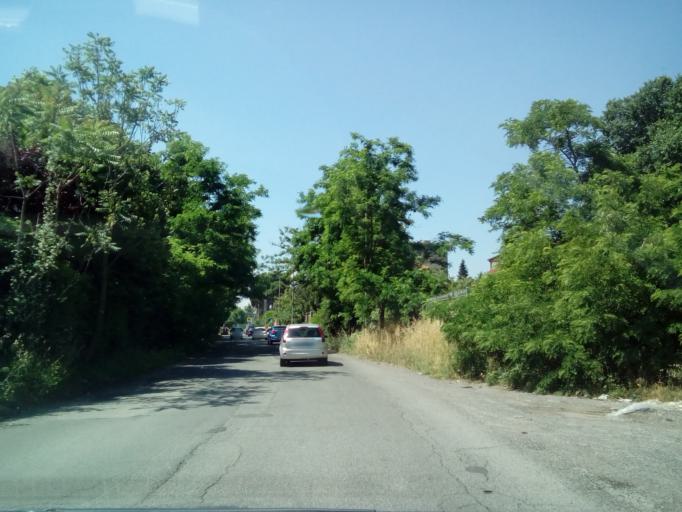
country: IT
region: Latium
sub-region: Citta metropolitana di Roma Capitale
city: Rome
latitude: 41.8775
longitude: 12.5893
